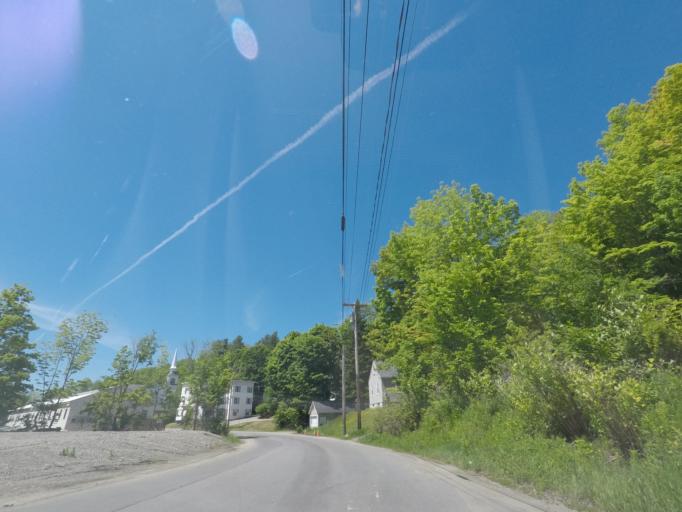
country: US
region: Maine
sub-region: Kennebec County
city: Gardiner
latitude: 44.2310
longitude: -69.7766
